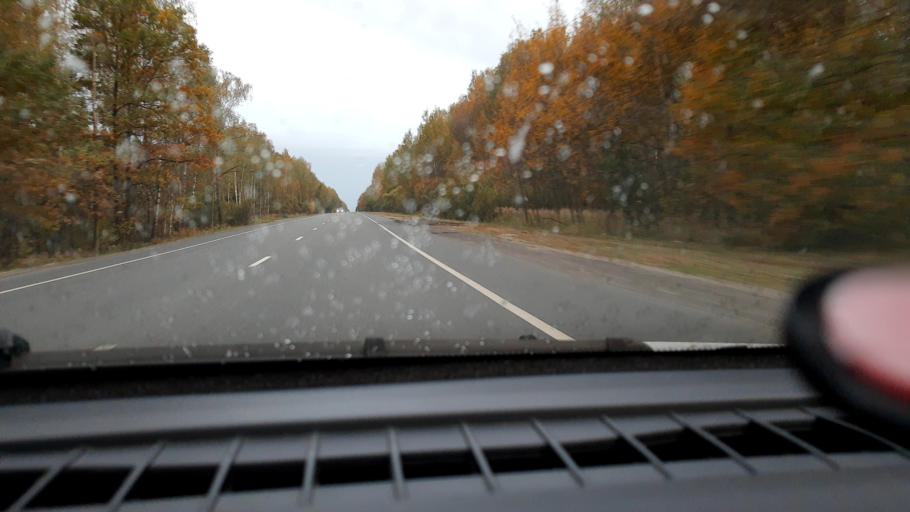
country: RU
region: Vladimir
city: Orgtrud
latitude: 56.2046
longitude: 40.7338
